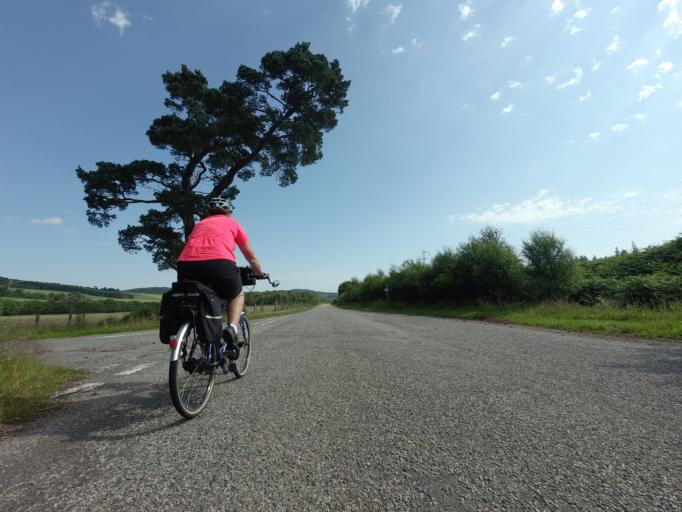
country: GB
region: Scotland
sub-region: Highland
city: Invergordon
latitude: 57.7411
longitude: -4.1803
